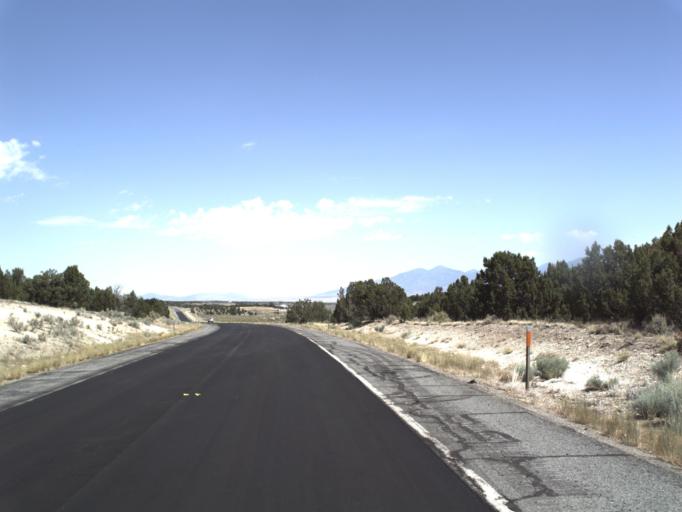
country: US
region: Utah
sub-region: Utah County
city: Eagle Mountain
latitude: 40.0080
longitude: -112.2761
